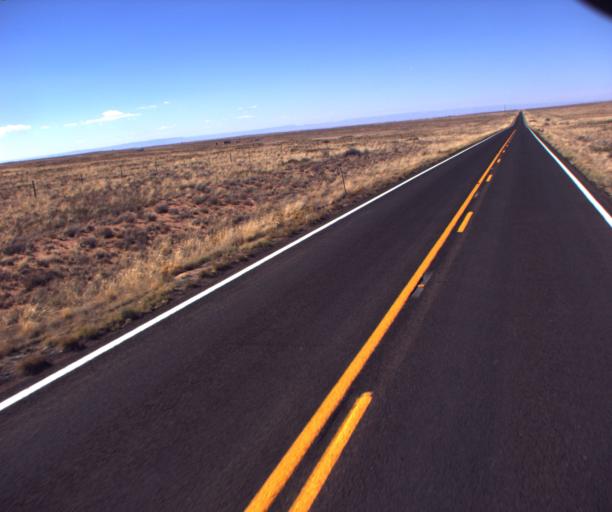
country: US
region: Arizona
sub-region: Coconino County
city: Tuba City
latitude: 35.9731
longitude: -110.9691
